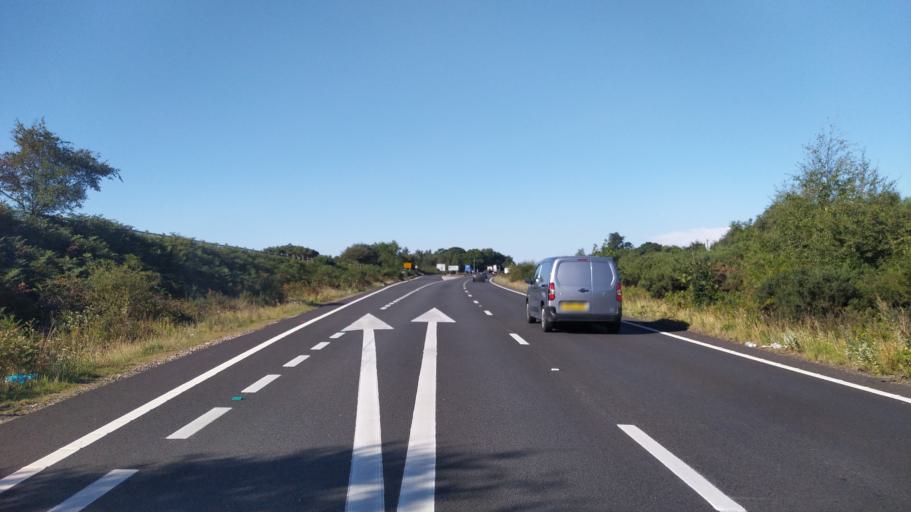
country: GB
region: England
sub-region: Hampshire
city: Ringwood
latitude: 50.8563
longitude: -1.7256
